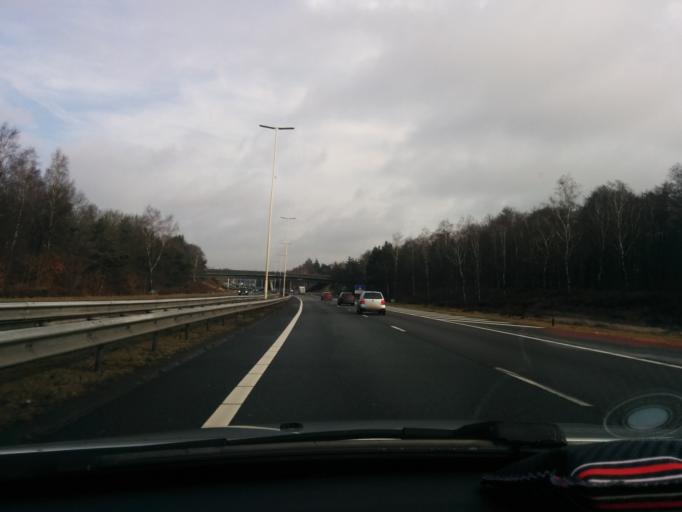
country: NL
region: North Holland
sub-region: Gemeente Hilversum
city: Hilversum
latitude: 52.1838
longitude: 5.1840
